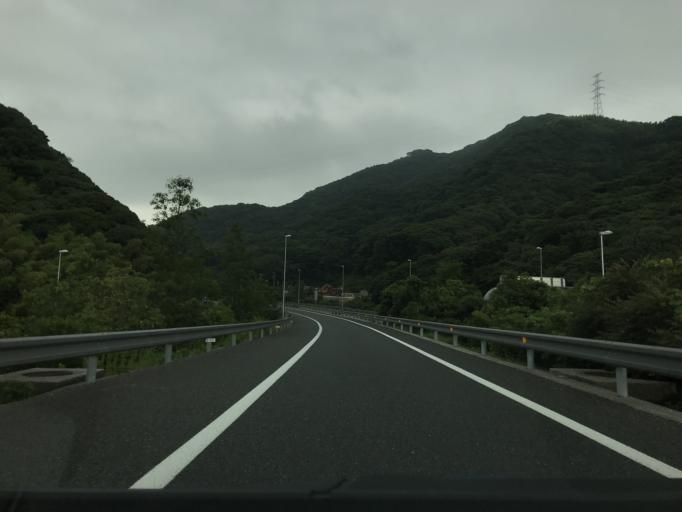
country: JP
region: Fukuoka
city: Kitakyushu
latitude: 33.8152
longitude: 130.8878
